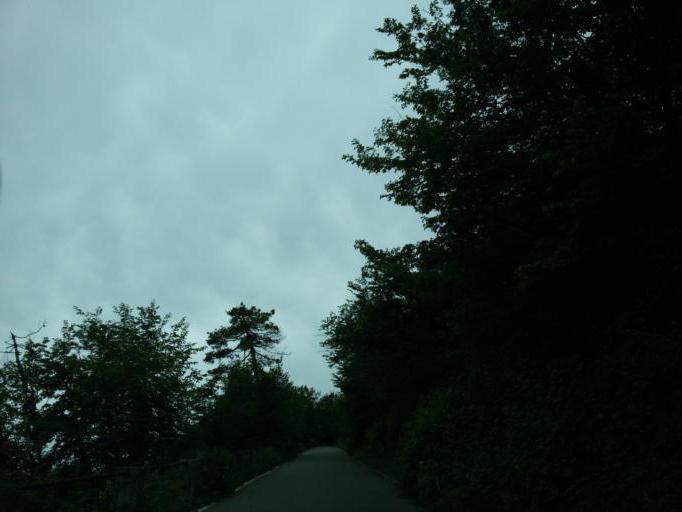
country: IT
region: Liguria
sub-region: Provincia di Genova
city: Genoa
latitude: 44.4392
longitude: 8.9245
